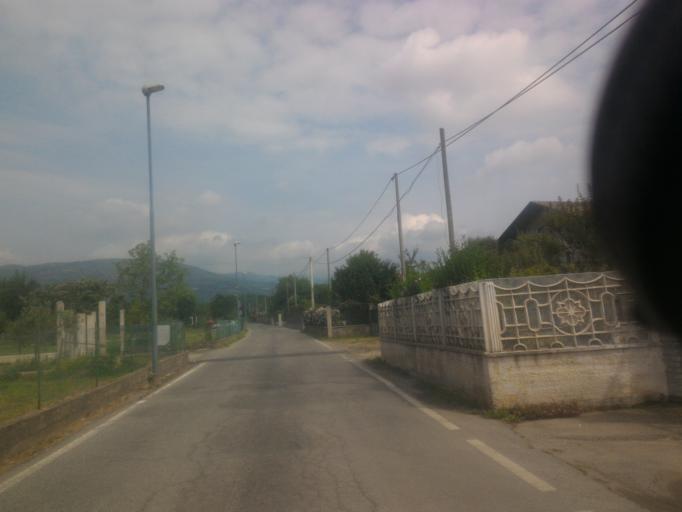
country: IT
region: Piedmont
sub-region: Provincia di Torino
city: Pinerolo
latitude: 44.8684
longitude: 7.3196
